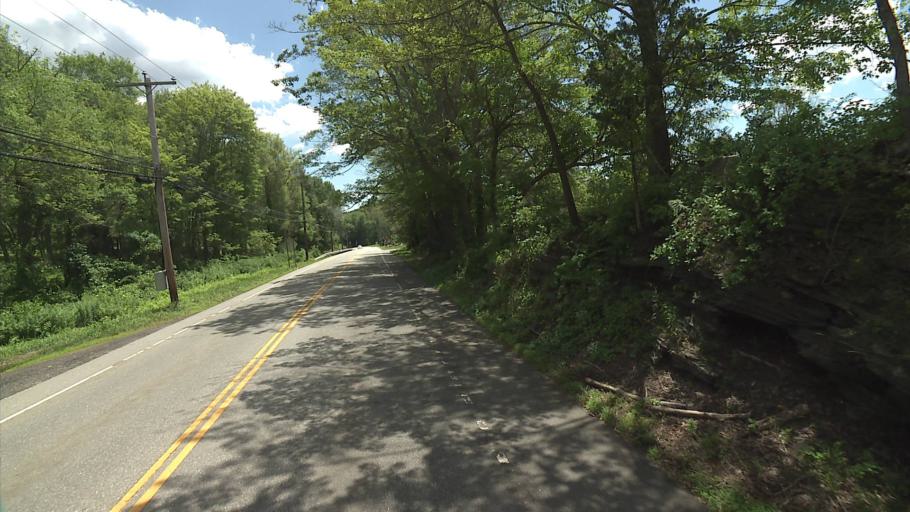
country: US
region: Connecticut
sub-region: Middlesex County
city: Moodus
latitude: 41.5049
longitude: -72.4761
